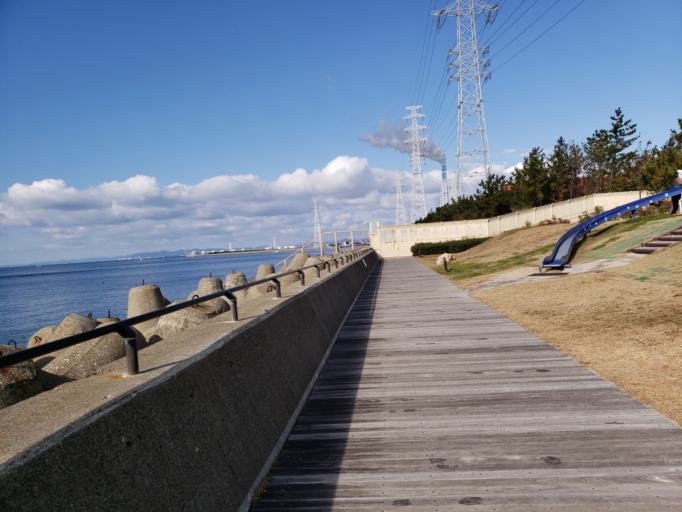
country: JP
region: Hyogo
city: Kakogawacho-honmachi
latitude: 34.7463
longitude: 134.7765
